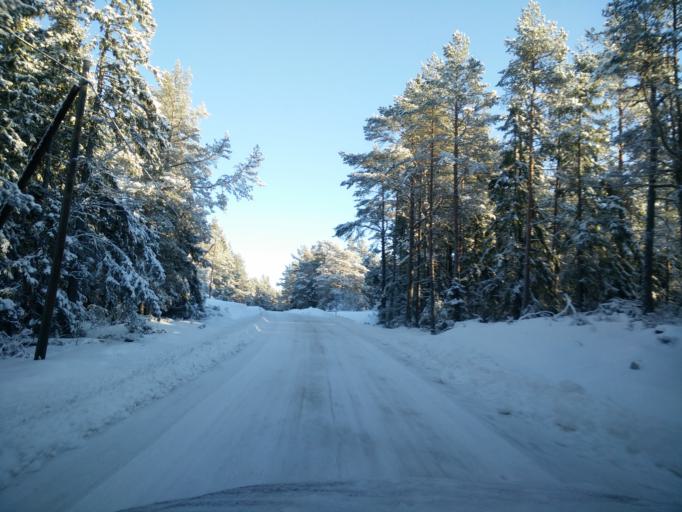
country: SE
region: Vaesternorrland
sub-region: Sundsvalls Kommun
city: Njurundabommen
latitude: 62.2329
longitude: 17.6341
